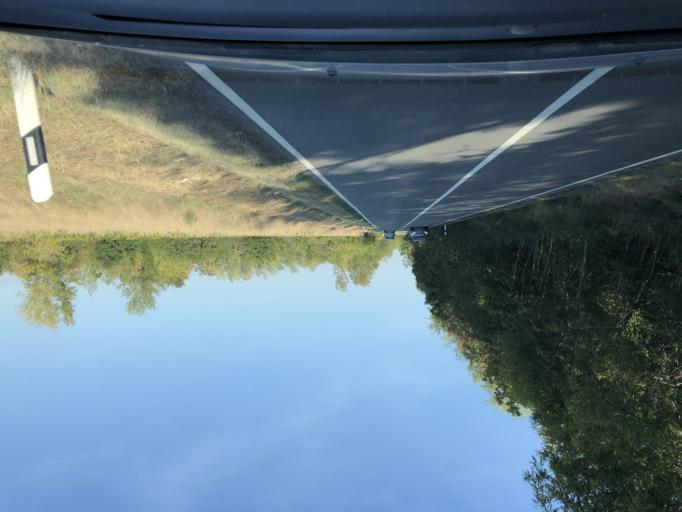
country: DE
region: Saxony-Anhalt
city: Grosskayna
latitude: 51.2847
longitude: 11.9197
